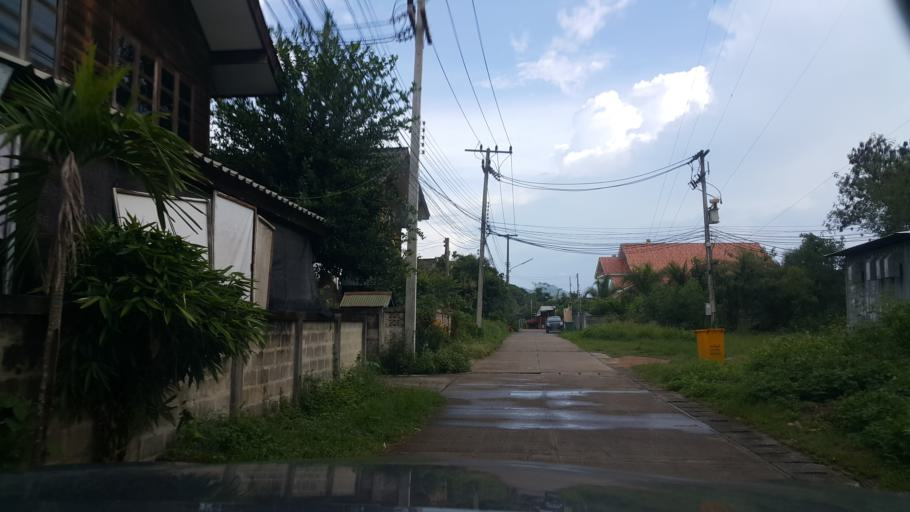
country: TH
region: Lampang
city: Thoen
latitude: 17.6099
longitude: 99.2161
